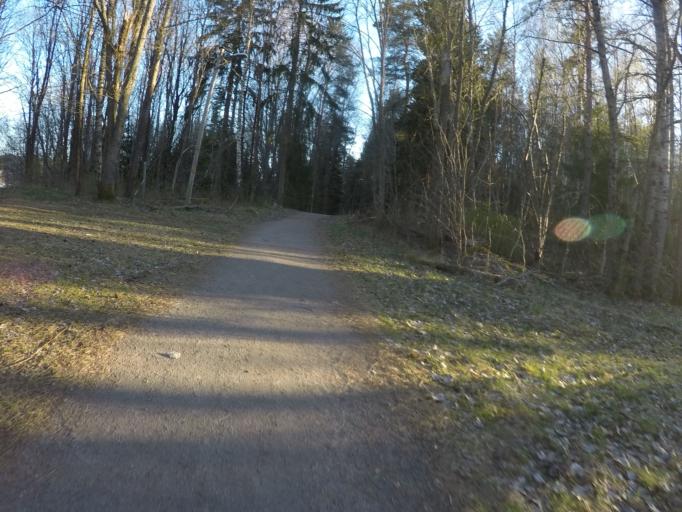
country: SE
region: Soedermanland
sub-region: Eskilstuna Kommun
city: Eskilstuna
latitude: 59.3949
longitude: 16.5274
